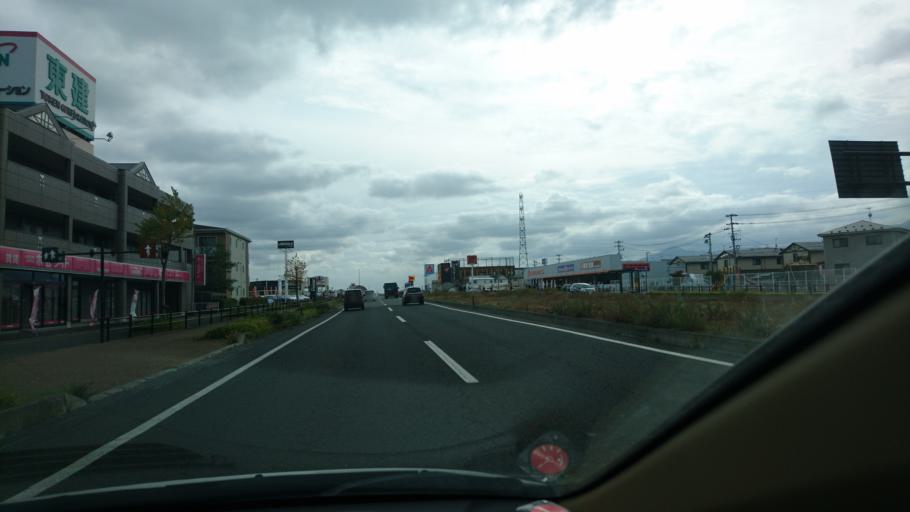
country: JP
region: Iwate
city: Morioka-shi
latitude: 39.6827
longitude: 141.1356
